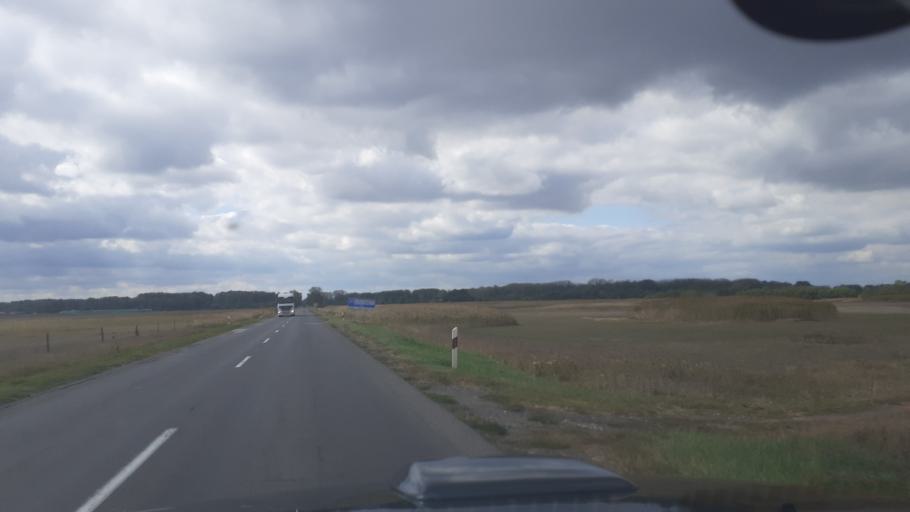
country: HU
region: Bacs-Kiskun
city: Fulopszallas
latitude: 46.8113
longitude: 19.1739
